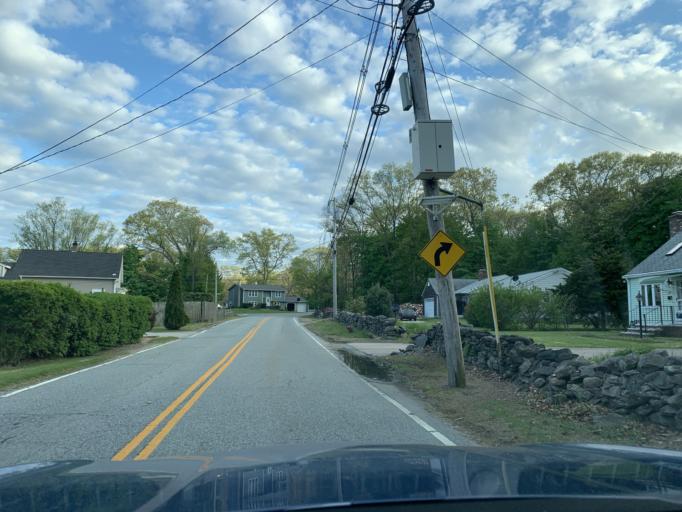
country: US
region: Rhode Island
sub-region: Kent County
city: East Greenwich
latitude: 41.6324
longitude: -71.4592
